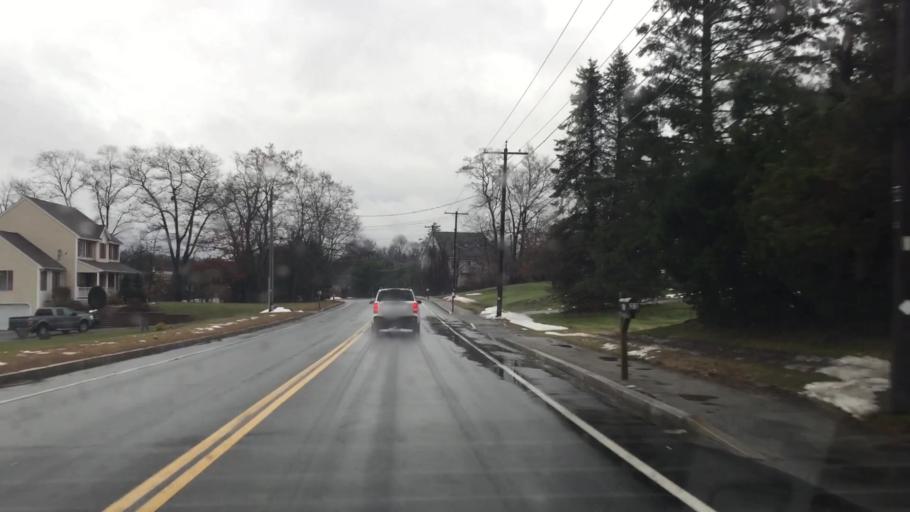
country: US
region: New Hampshire
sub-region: Rockingham County
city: Salem
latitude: 42.7569
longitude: -71.2162
